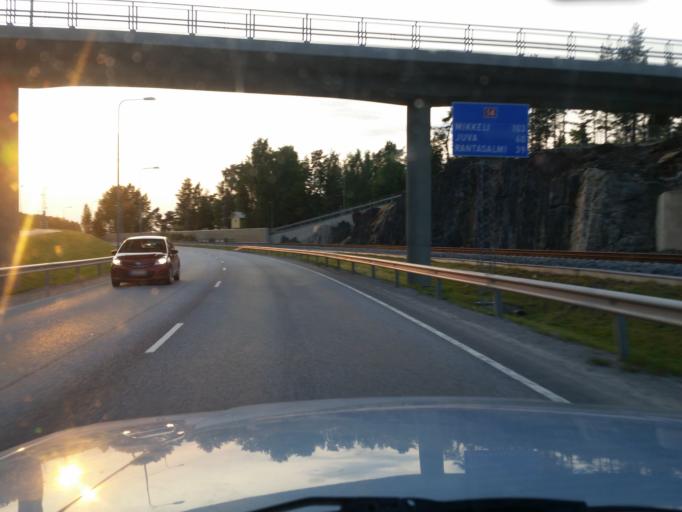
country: FI
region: Southern Savonia
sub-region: Savonlinna
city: Savonlinna
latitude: 61.8787
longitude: 28.8719
